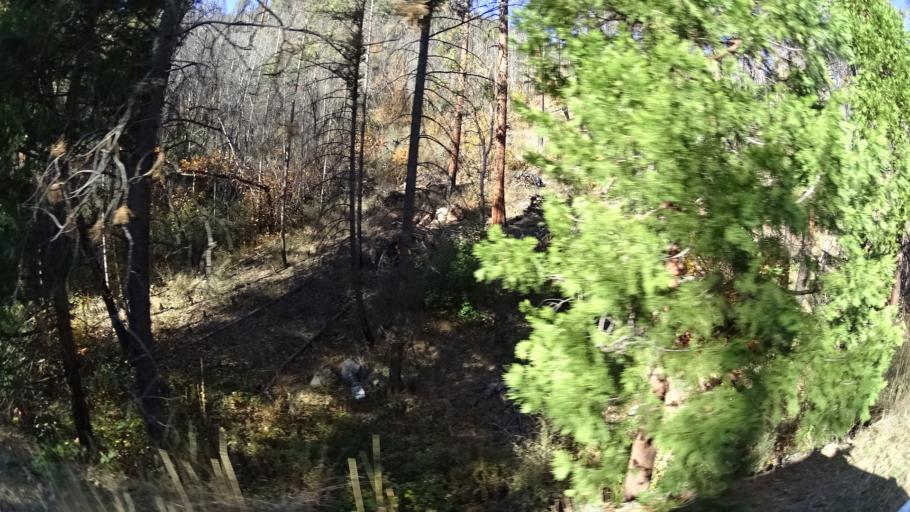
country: US
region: California
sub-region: Siskiyou County
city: Yreka
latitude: 41.8866
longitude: -122.8232
